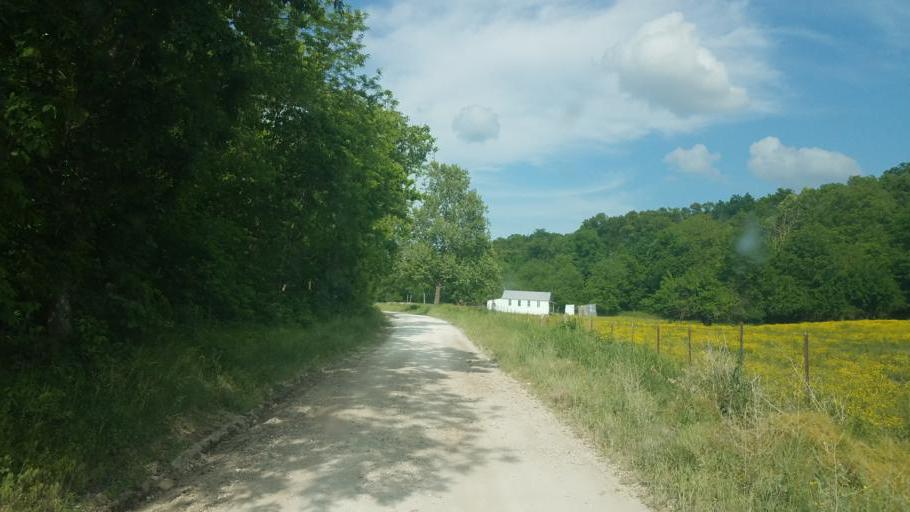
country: US
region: Missouri
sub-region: Cooper County
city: Boonville
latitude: 38.8476
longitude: -92.6548
